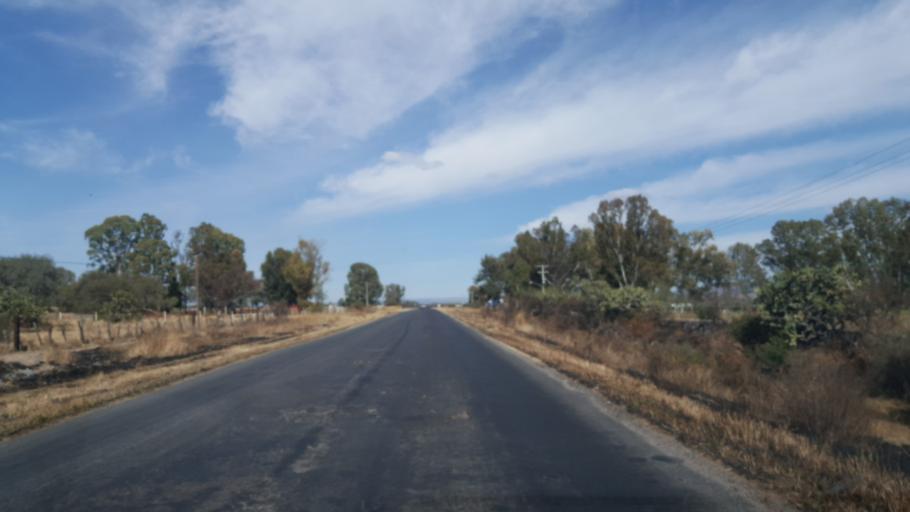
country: MX
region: Jalisco
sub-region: Lagos de Moreno
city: Geovillas Laureles del Campanario
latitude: 21.2884
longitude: -101.9327
